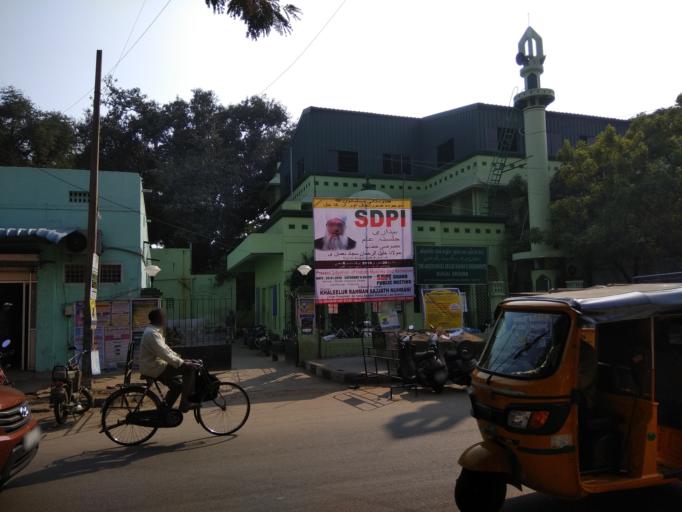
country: IN
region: Tamil Nadu
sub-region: Chennai
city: Chetput
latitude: 13.0537
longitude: 80.2674
